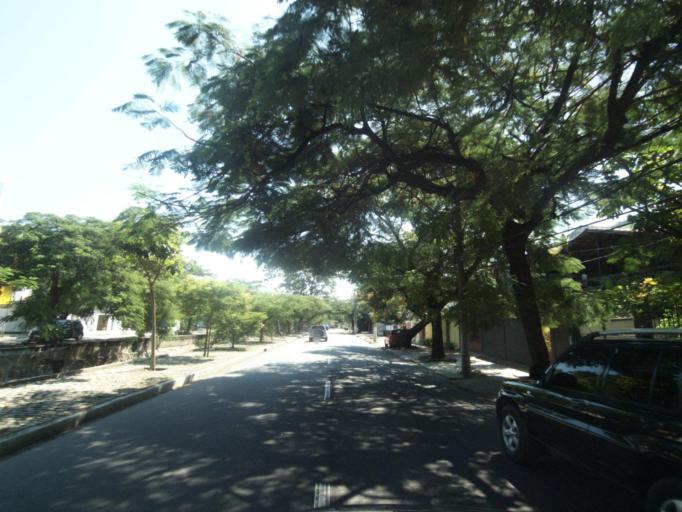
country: BR
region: Rio de Janeiro
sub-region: Niteroi
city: Niteroi
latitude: -22.9144
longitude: -43.0928
